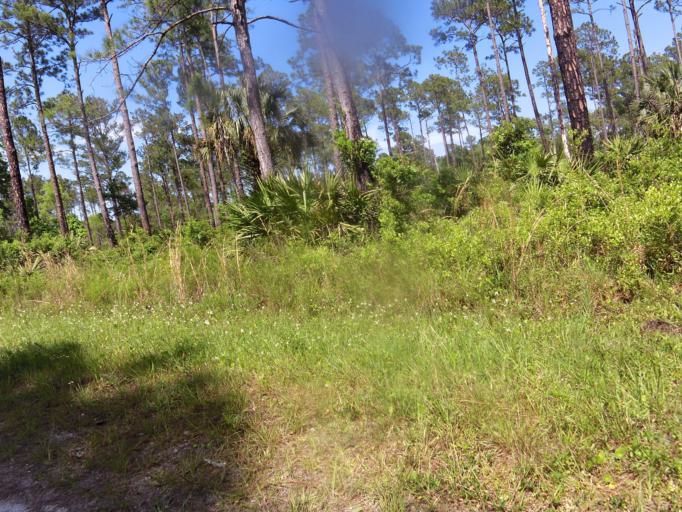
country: US
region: Florida
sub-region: Saint Johns County
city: Palm Valley
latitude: 30.1405
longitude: -81.3761
